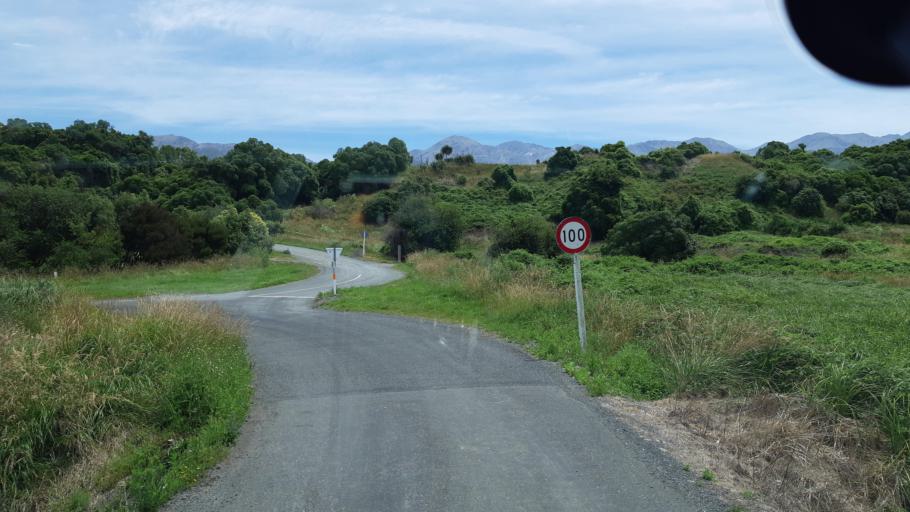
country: NZ
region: Canterbury
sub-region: Kaikoura District
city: Kaikoura
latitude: -42.3331
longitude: 173.7225
